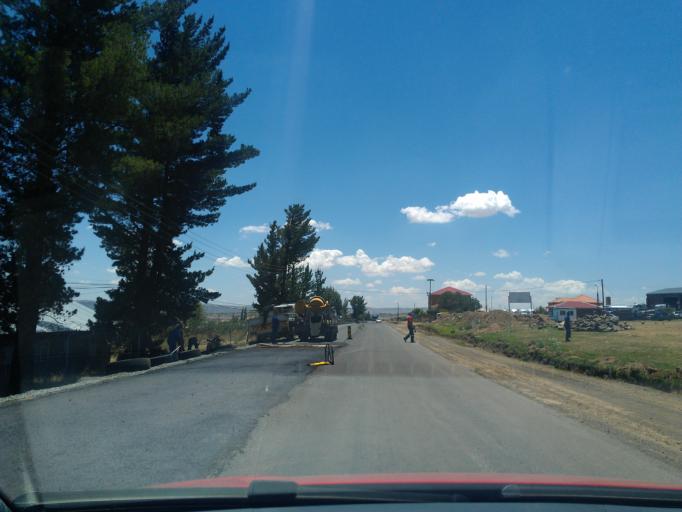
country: LS
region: Berea
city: Teyateyaneng
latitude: -29.1410
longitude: 27.7636
